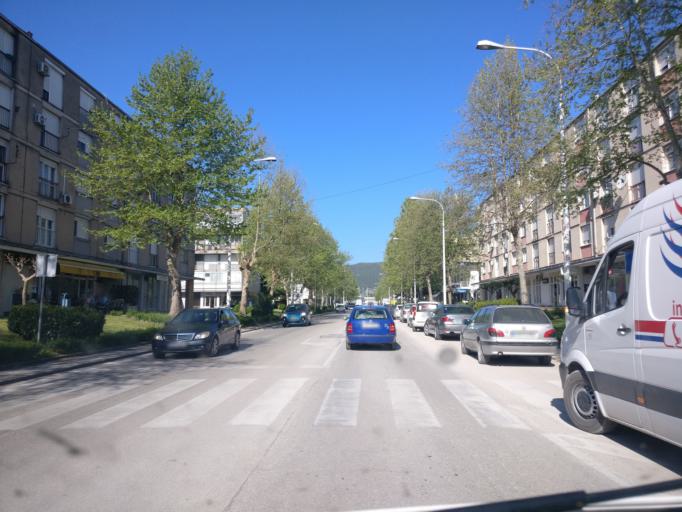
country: BA
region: Federation of Bosnia and Herzegovina
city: Tasovcici
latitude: 43.1094
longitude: 17.7038
